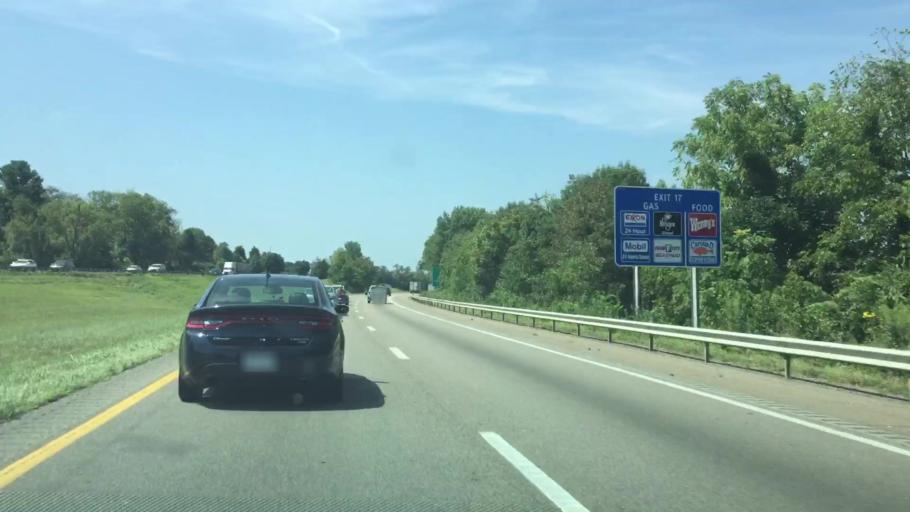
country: US
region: Virginia
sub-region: Washington County
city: Abingdon
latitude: 36.7031
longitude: -81.9592
